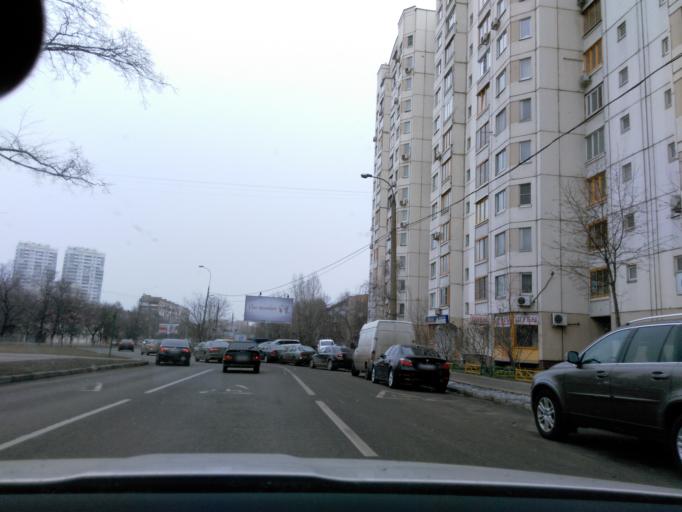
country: RU
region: Moscow
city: Novyye Cheremushki
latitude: 55.6834
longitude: 37.5854
